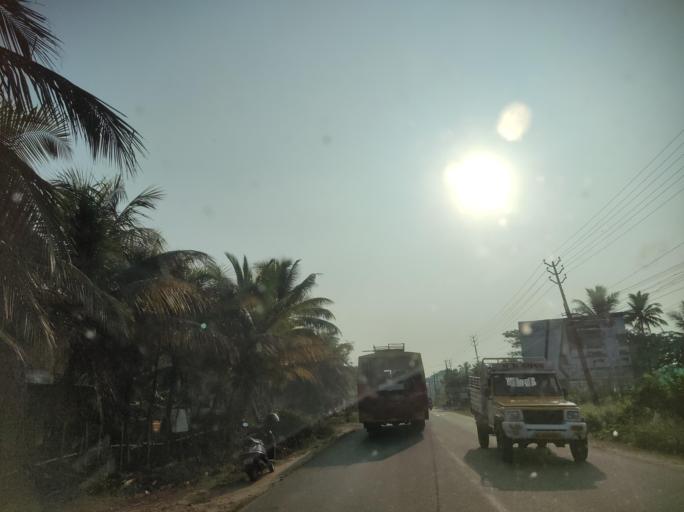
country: IN
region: Kerala
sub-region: Kottayam
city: Kottayam
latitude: 9.5923
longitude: 76.4417
